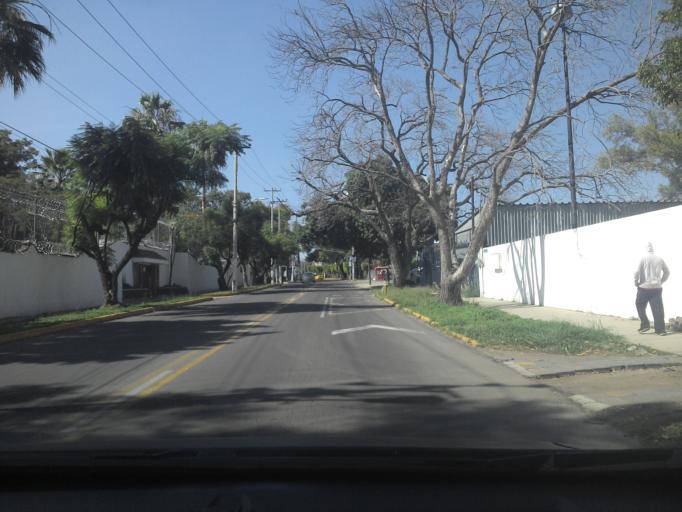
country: MX
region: Jalisco
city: Zapopan2
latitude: 20.6919
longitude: -103.4088
